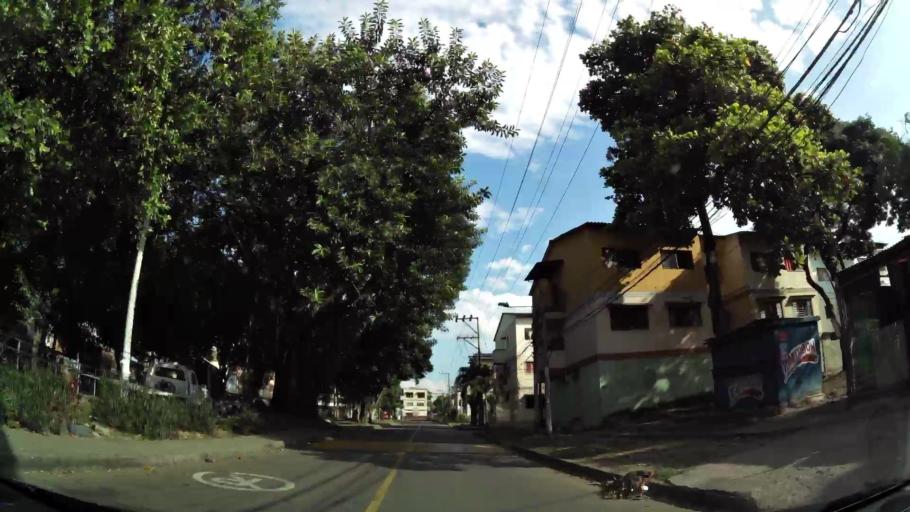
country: CO
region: Valle del Cauca
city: Cali
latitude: 3.4685
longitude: -76.5160
